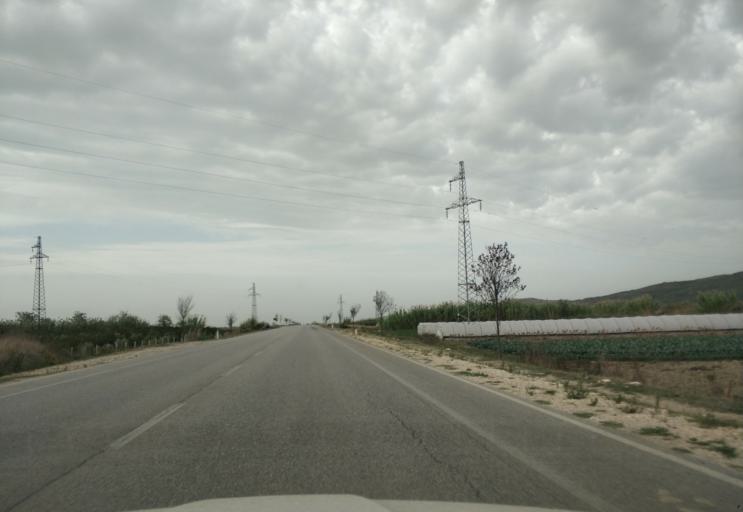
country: AL
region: Fier
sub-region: Rrethi i Fierit
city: Frakulla e Madhe
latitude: 40.6384
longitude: 19.5030
